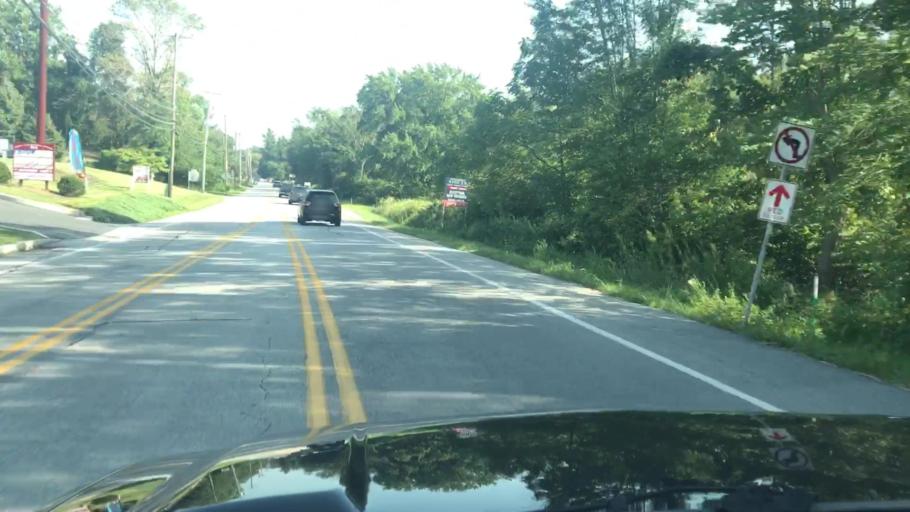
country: US
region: Pennsylvania
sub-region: York County
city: Valley Green
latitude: 40.1766
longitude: -76.8322
